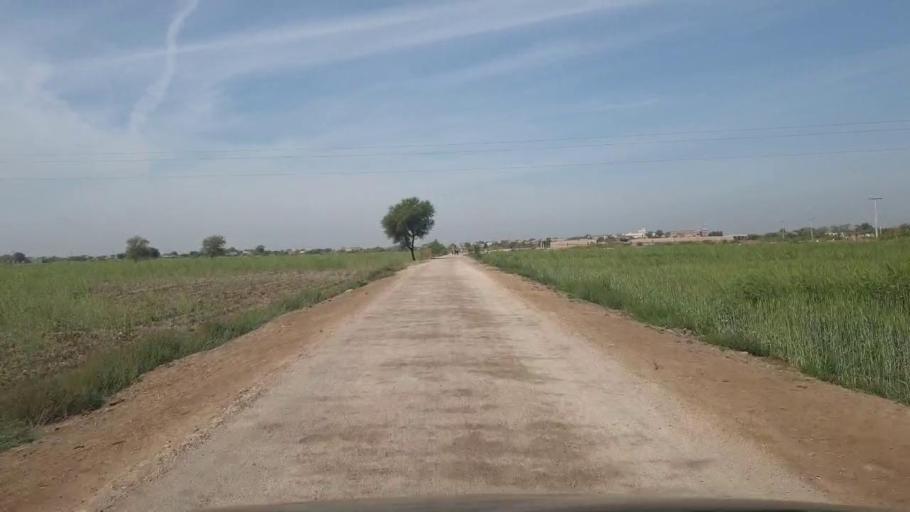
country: PK
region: Sindh
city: Umarkot
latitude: 25.3521
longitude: 69.5946
